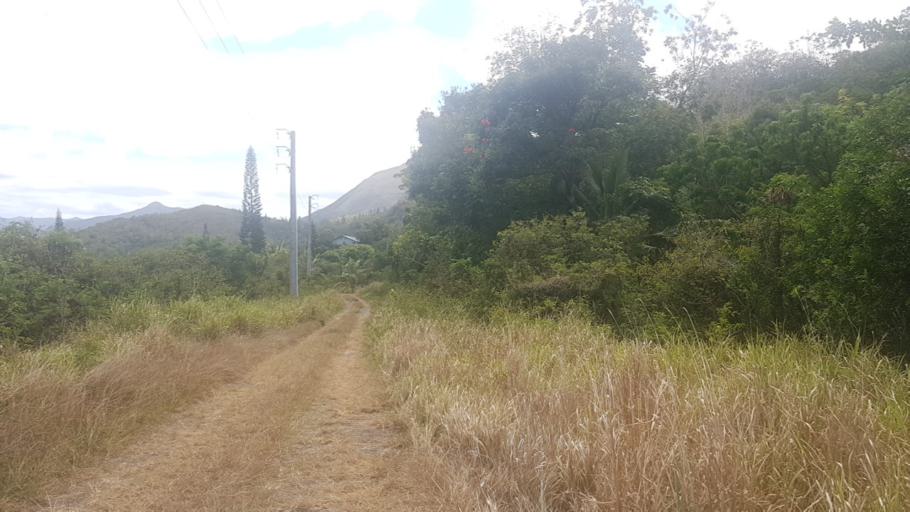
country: NC
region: South Province
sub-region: Dumbea
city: Dumbea
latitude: -22.1850
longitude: 166.4792
